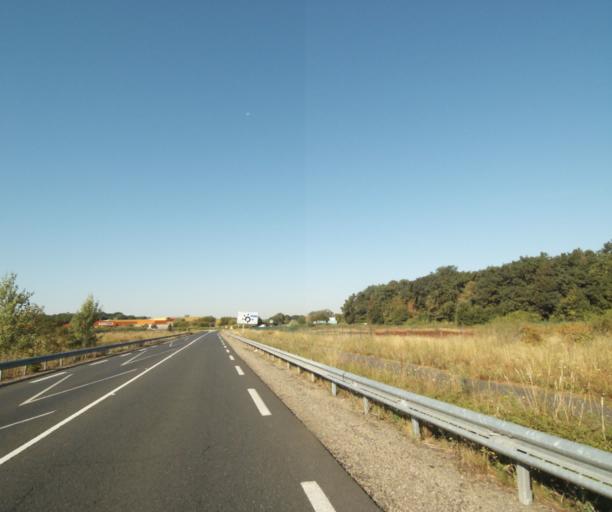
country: FR
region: Ile-de-France
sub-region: Departement de Seine-et-Marne
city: Savigny-le-Temple
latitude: 48.5910
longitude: 2.6037
